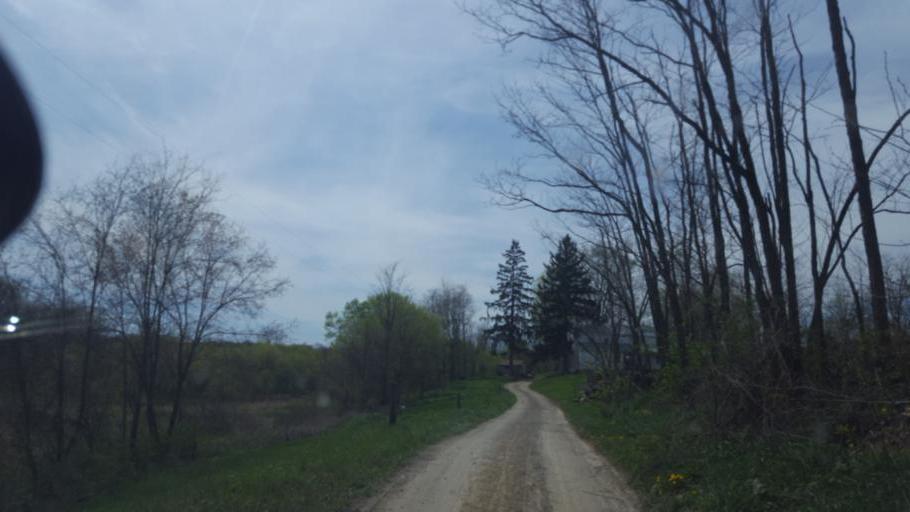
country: US
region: Ohio
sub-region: Ashland County
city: Ashland
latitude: 40.9110
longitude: -82.3602
